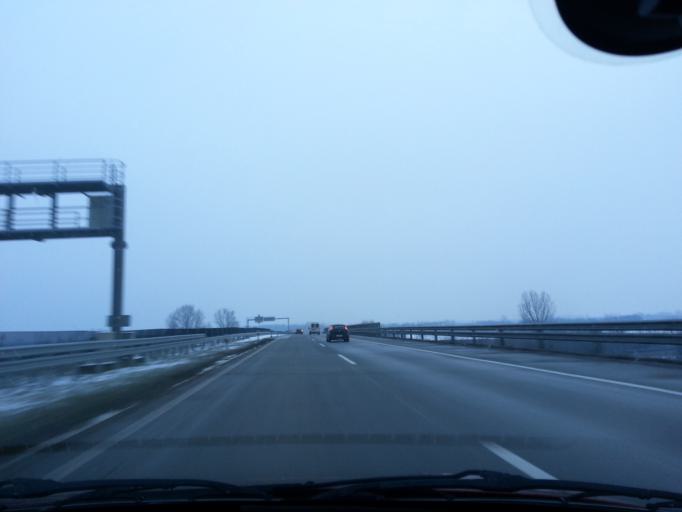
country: HU
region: Pest
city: Vecses
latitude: 47.3950
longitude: 19.3033
